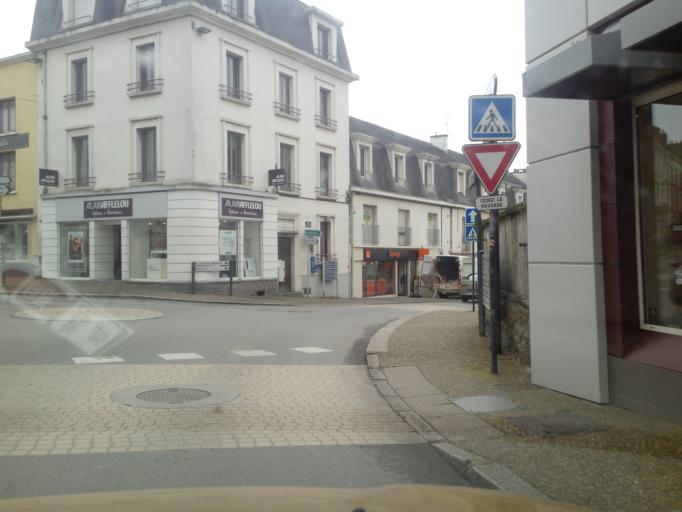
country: FR
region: Brittany
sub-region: Departement du Morbihan
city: Ploermel
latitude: 47.9318
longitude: -2.3988
